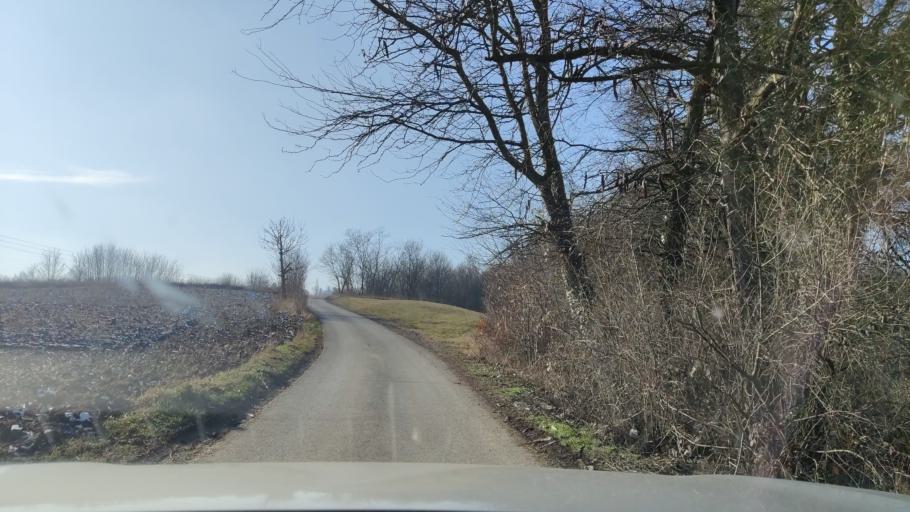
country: RS
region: Central Serbia
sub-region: Belgrade
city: Zvezdara
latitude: 44.7135
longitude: 20.5146
